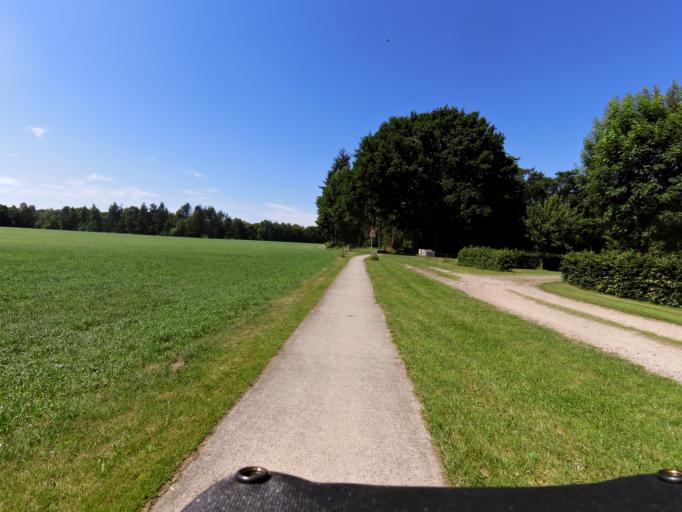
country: NL
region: Overijssel
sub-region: Gemeente Twenterand
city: Den Ham
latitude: 52.4902
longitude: 6.4923
